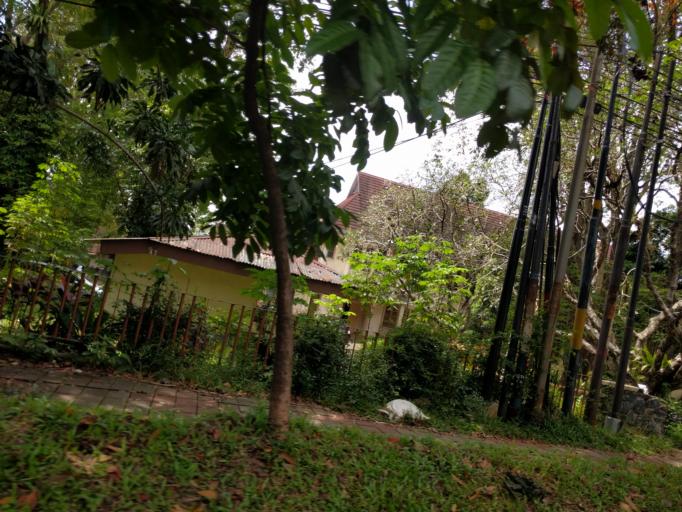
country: ID
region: West Java
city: Bogor
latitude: -6.5876
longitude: 106.8054
